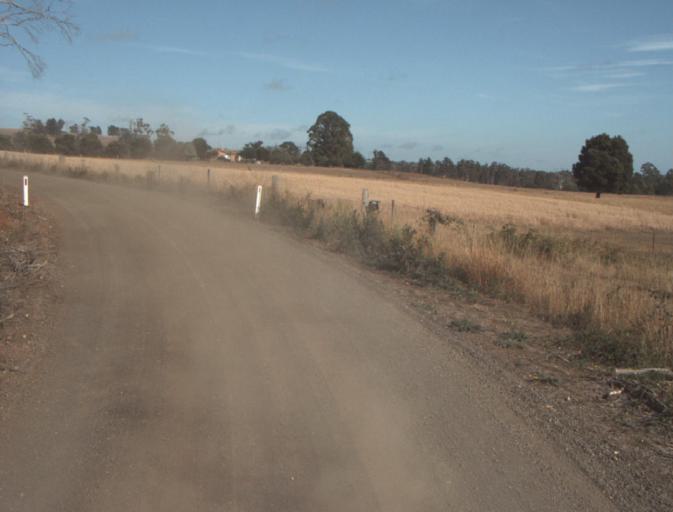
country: AU
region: Tasmania
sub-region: Dorset
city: Bridport
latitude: -41.1466
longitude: 147.2218
